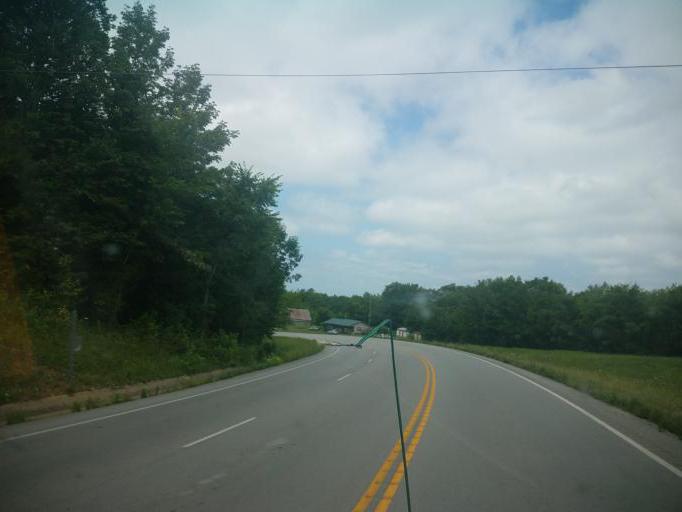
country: US
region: Kentucky
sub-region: Metcalfe County
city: Edmonton
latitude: 36.8843
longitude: -85.6959
